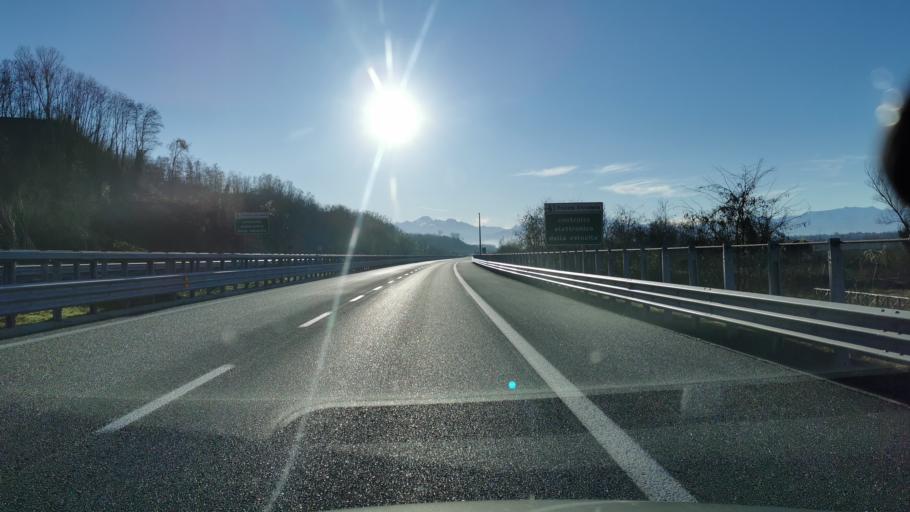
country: IT
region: Piedmont
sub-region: Provincia di Cuneo
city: Montanera
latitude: 44.4611
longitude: 7.6599
